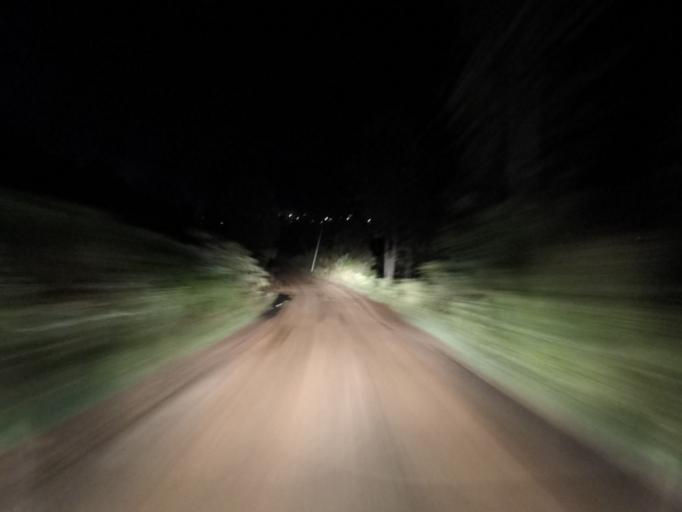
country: IN
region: Tamil Nadu
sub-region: Nilgiri
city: Kotagiri
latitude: 11.4552
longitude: 76.8080
